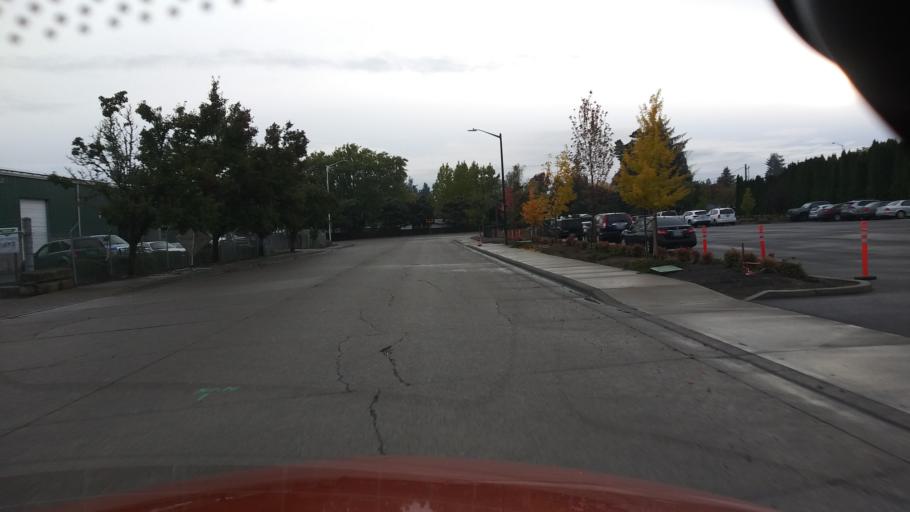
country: US
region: Oregon
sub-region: Washington County
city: Cornelius
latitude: 45.5265
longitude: -123.0609
